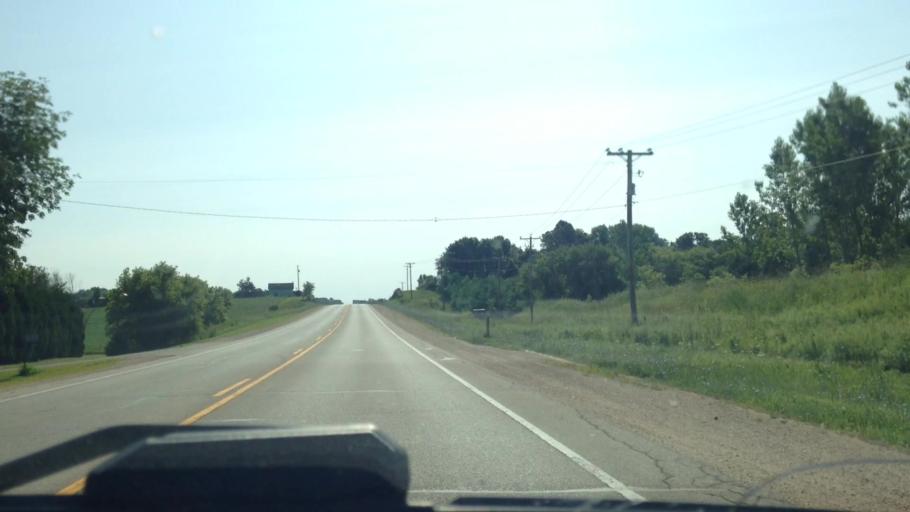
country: US
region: Wisconsin
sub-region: Dodge County
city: Mayville
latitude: 43.4430
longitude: -88.5592
